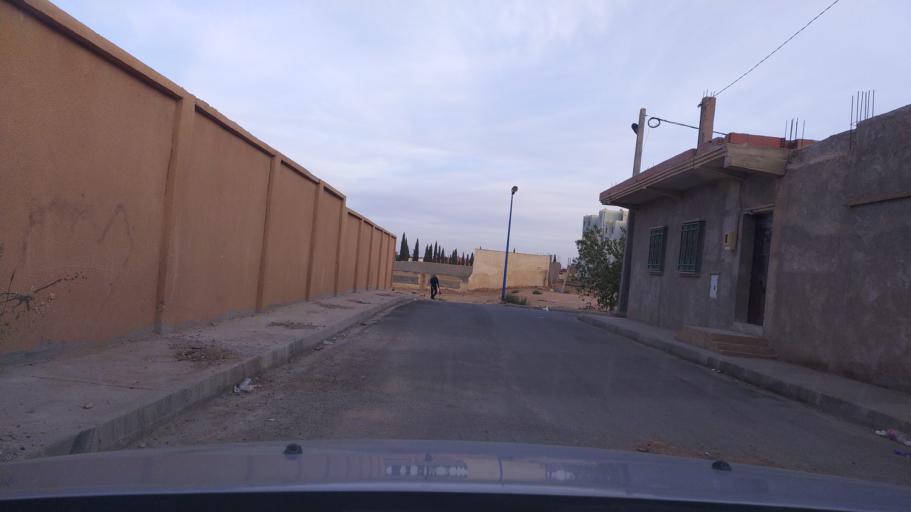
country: DZ
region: Tiaret
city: Frenda
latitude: 34.8956
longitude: 1.2395
